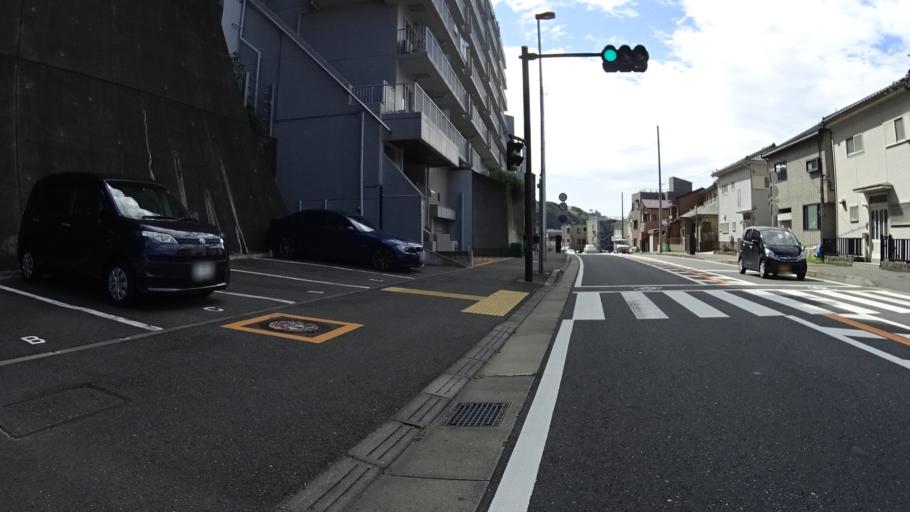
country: JP
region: Kanagawa
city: Yokosuka
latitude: 35.2528
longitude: 139.7110
